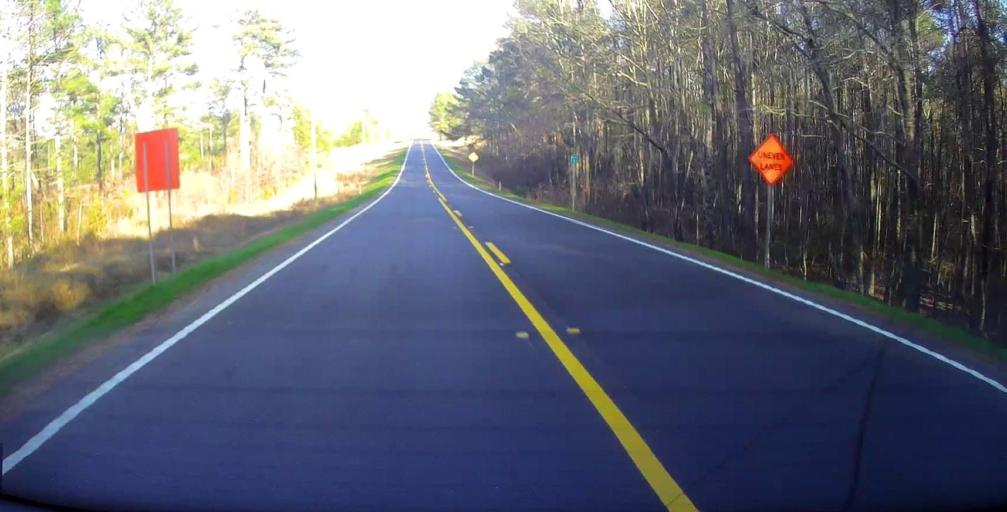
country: US
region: Georgia
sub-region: Harris County
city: Hamilton
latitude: 32.7472
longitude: -84.9876
